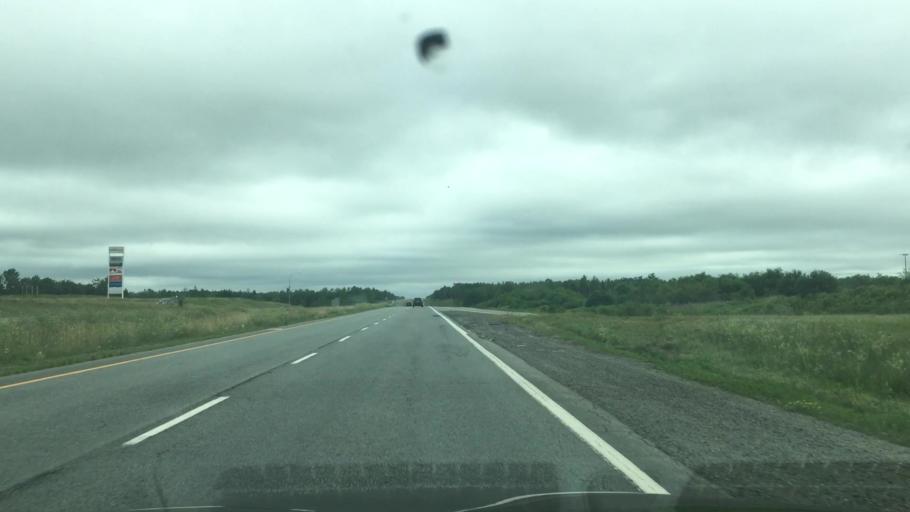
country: CA
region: Nova Scotia
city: Cole Harbour
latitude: 44.9784
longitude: -63.5073
